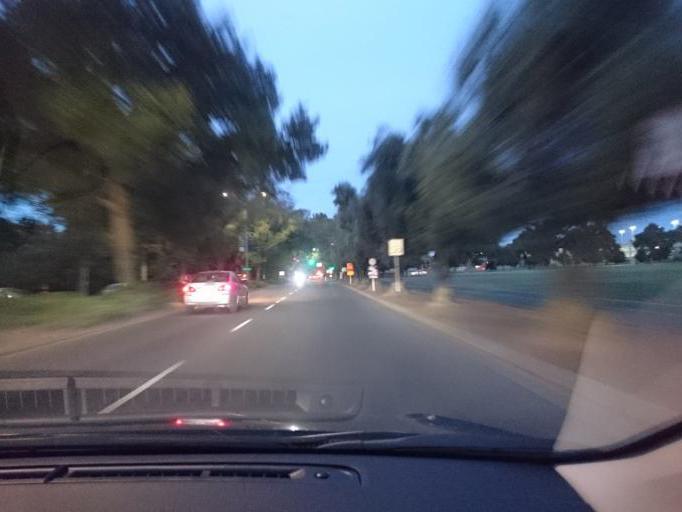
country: US
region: California
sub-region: Yolo County
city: Davis
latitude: 38.5461
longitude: -121.7525
